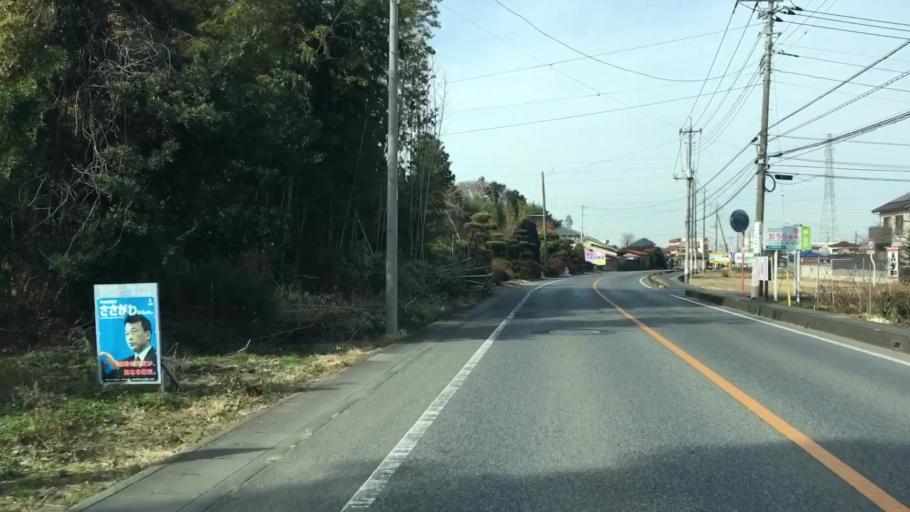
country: JP
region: Saitama
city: Menuma
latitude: 36.2489
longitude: 139.4315
